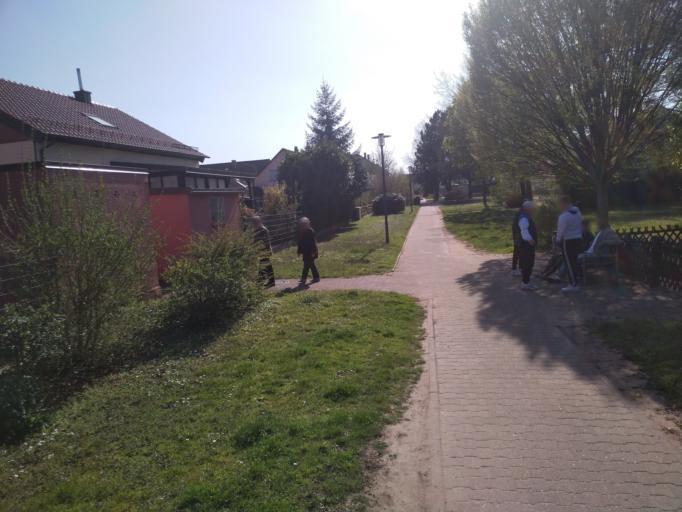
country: DE
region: Rheinland-Pfalz
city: Worth am Rhein
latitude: 49.0324
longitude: 8.2823
